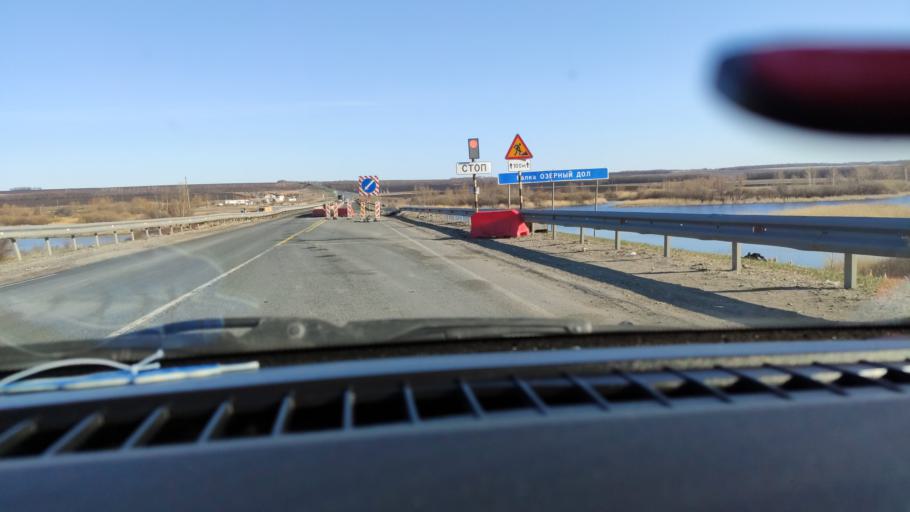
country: RU
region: Saratov
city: Dukhovnitskoye
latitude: 52.7362
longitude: 48.2562
